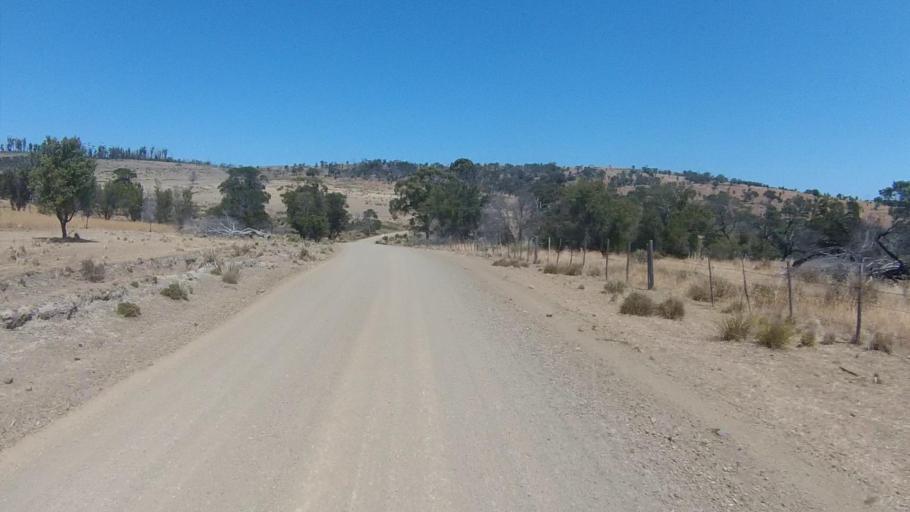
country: AU
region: Tasmania
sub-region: Sorell
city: Sorell
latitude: -42.8945
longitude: 147.8408
